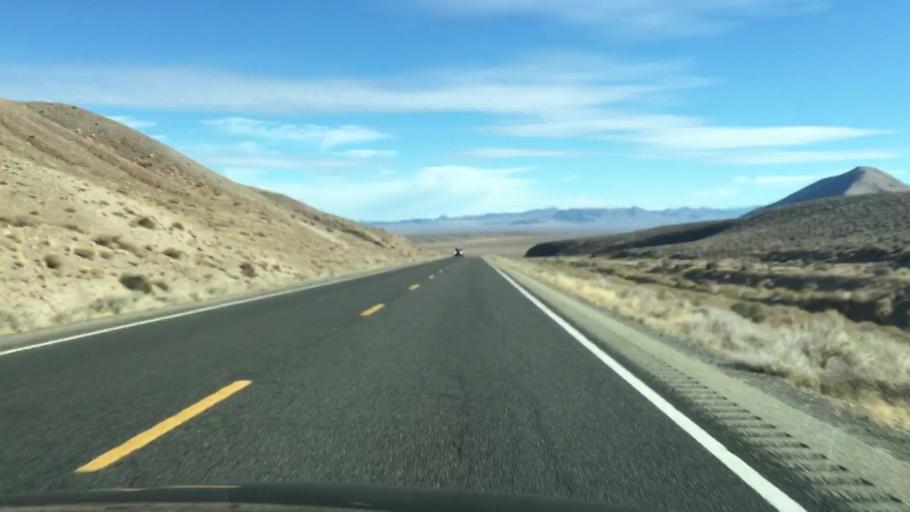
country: US
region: Nevada
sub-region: Lyon County
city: Yerington
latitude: 39.0380
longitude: -118.9327
